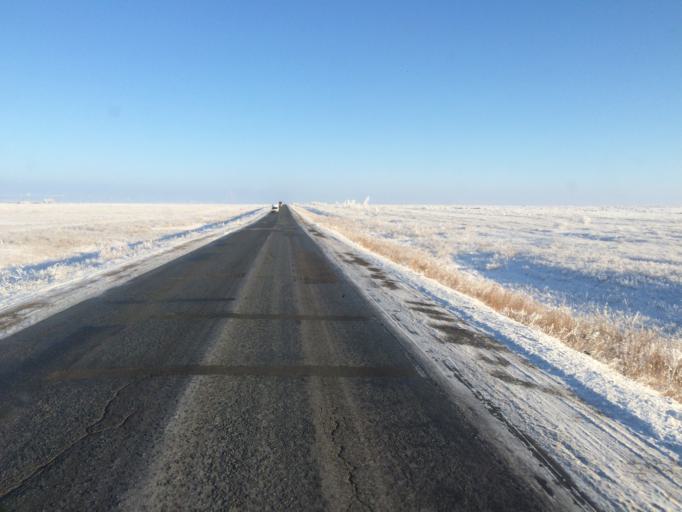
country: RU
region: Orenburg
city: Dombarovskiy
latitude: 50.1129
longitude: 59.2750
